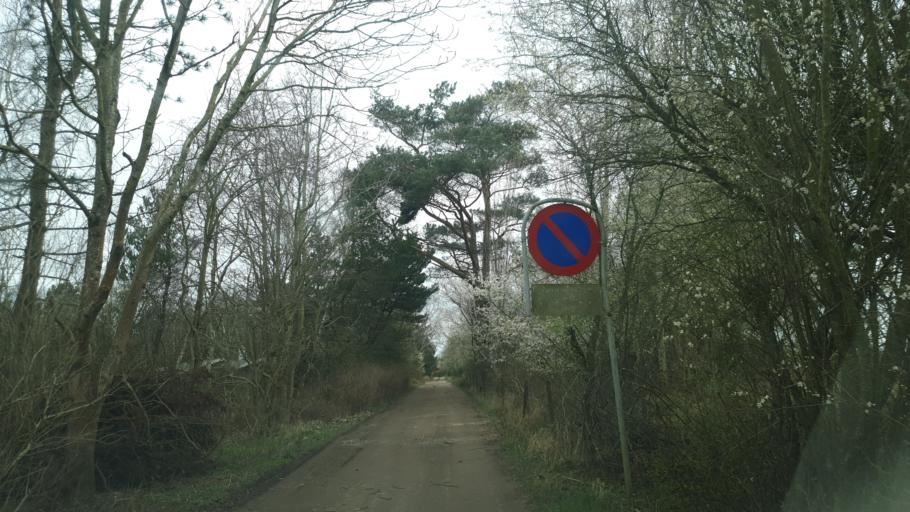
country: DK
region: Zealand
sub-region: Odsherred Kommune
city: Asnaes
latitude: 55.8340
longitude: 11.4200
